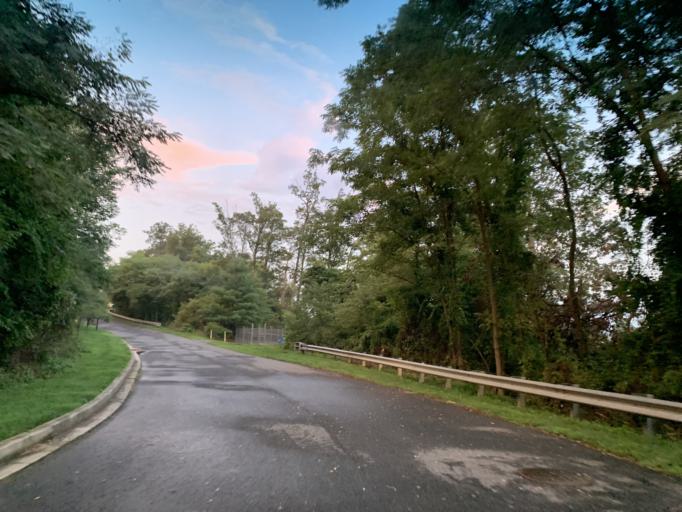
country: US
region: Maryland
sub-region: Harford County
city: Edgewood
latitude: 39.3969
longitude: -76.3460
